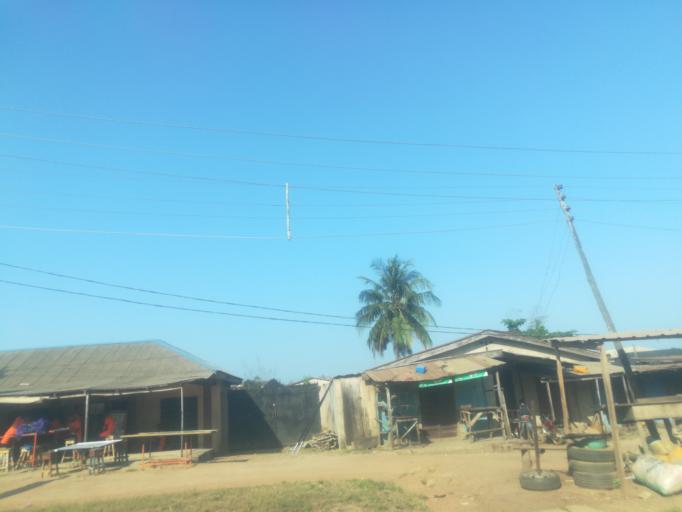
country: NG
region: Ogun
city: Abeokuta
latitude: 7.1749
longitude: 3.2894
